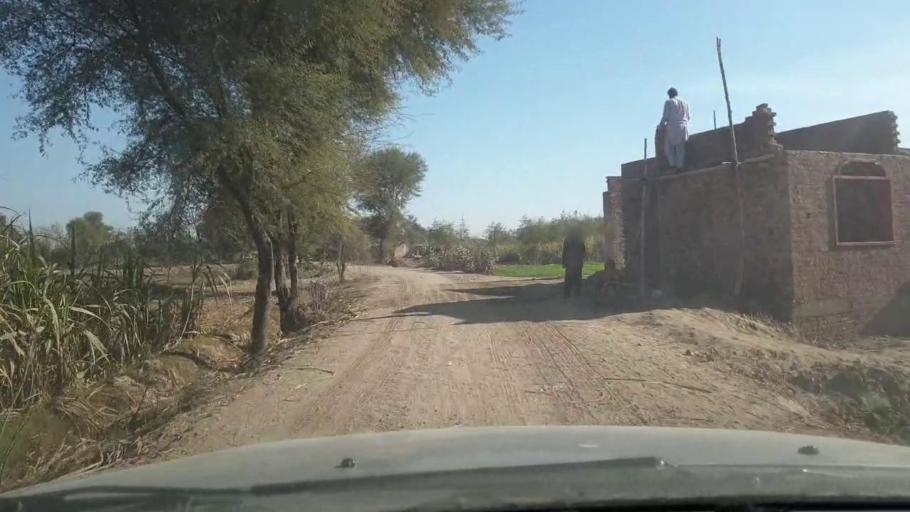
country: PK
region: Sindh
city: Ghotki
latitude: 27.9726
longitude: 69.1919
